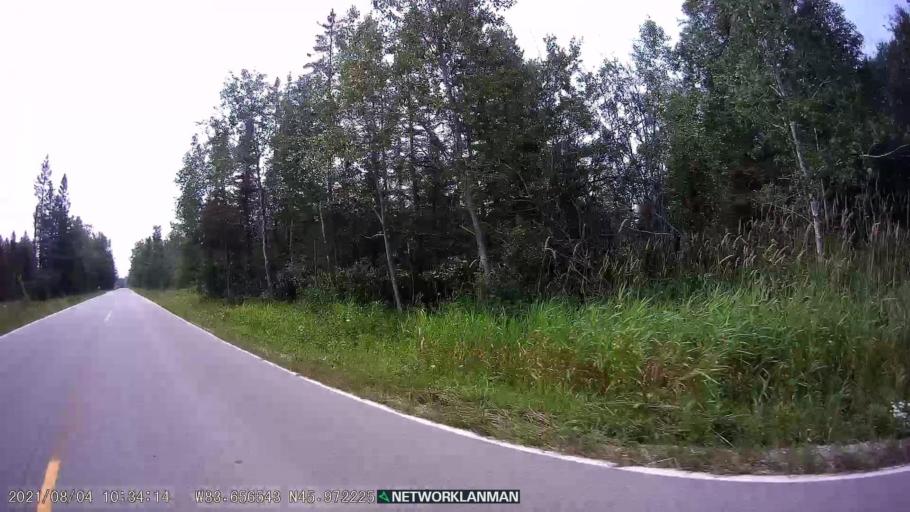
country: CA
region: Ontario
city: Thessalon
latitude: 45.9720
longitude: -83.6565
